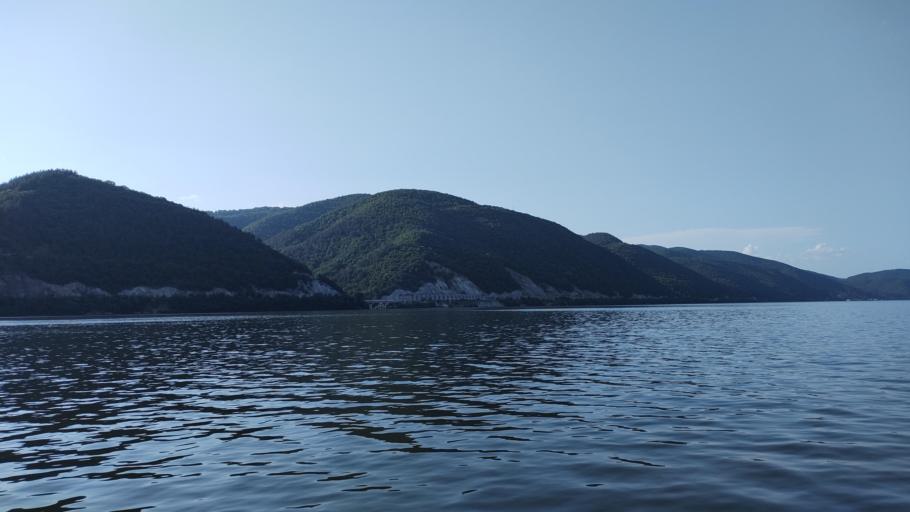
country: RO
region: Mehedinti
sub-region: Comuna Dubova
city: Dubova
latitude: 44.5354
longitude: 22.2157
